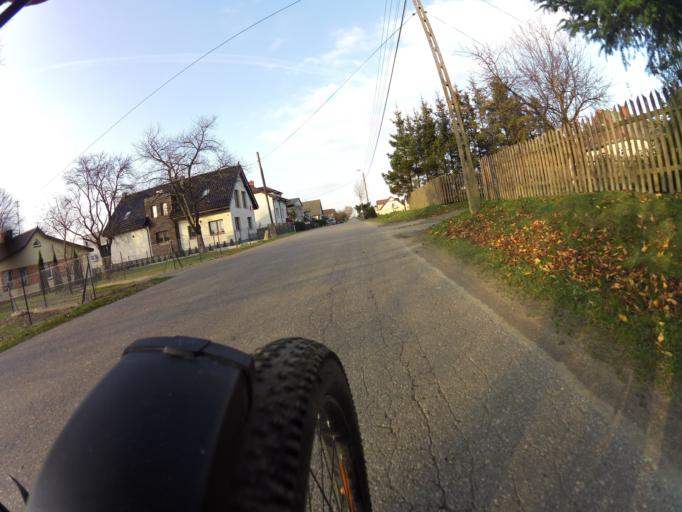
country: PL
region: Pomeranian Voivodeship
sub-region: Powiat pucki
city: Krokowa
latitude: 54.7632
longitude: 18.1817
